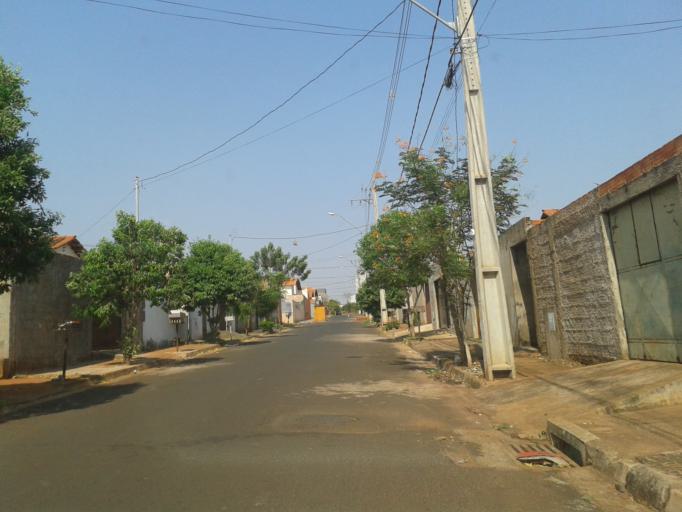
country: BR
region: Minas Gerais
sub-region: Ituiutaba
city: Ituiutaba
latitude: -18.9853
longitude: -49.4274
